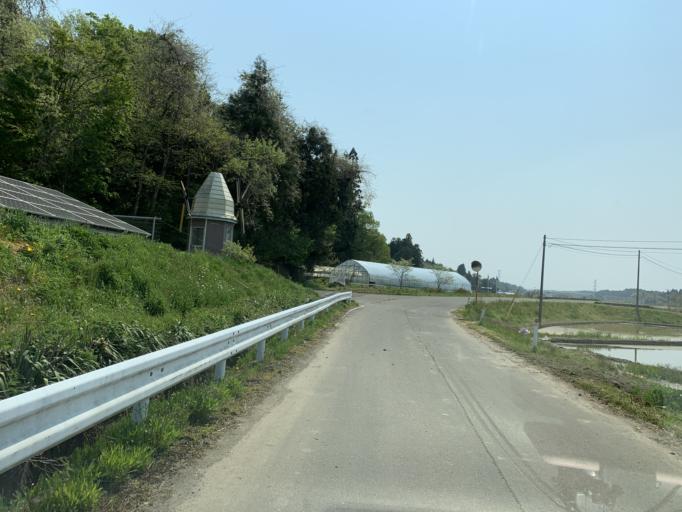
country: JP
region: Iwate
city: Ichinoseki
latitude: 38.8629
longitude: 141.0610
